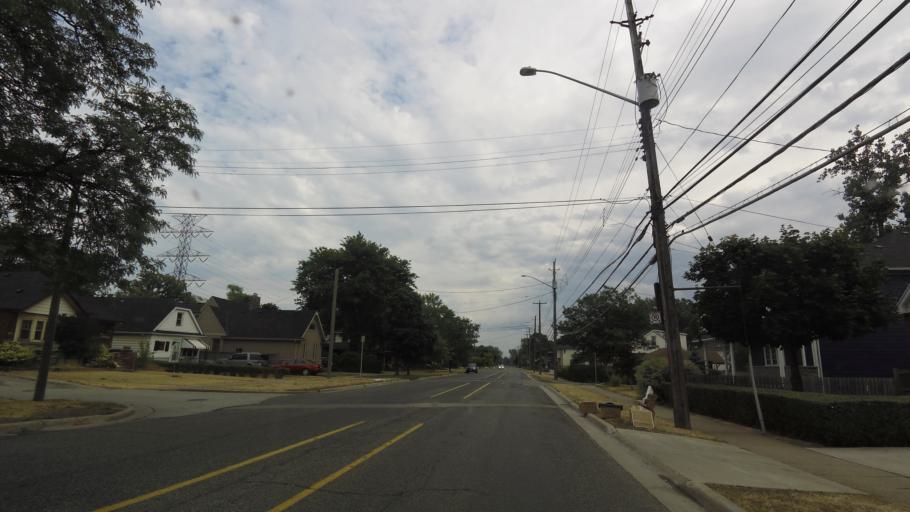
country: CA
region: Ontario
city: Hamilton
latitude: 43.2788
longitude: -79.7836
